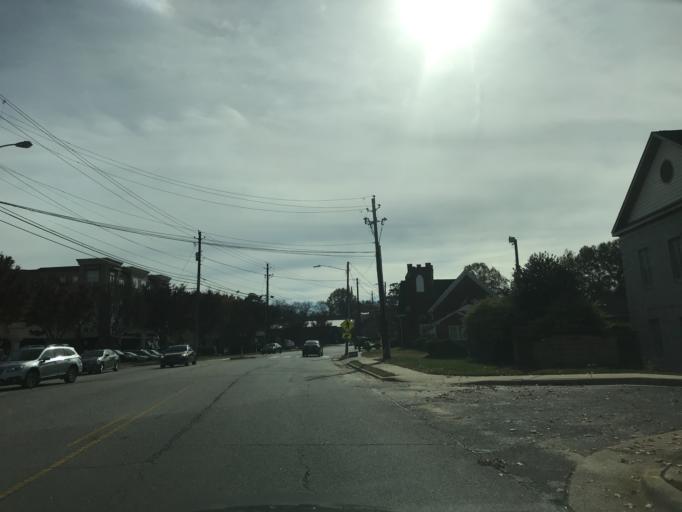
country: US
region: North Carolina
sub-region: Wake County
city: West Raleigh
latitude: 35.7985
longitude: -78.6602
